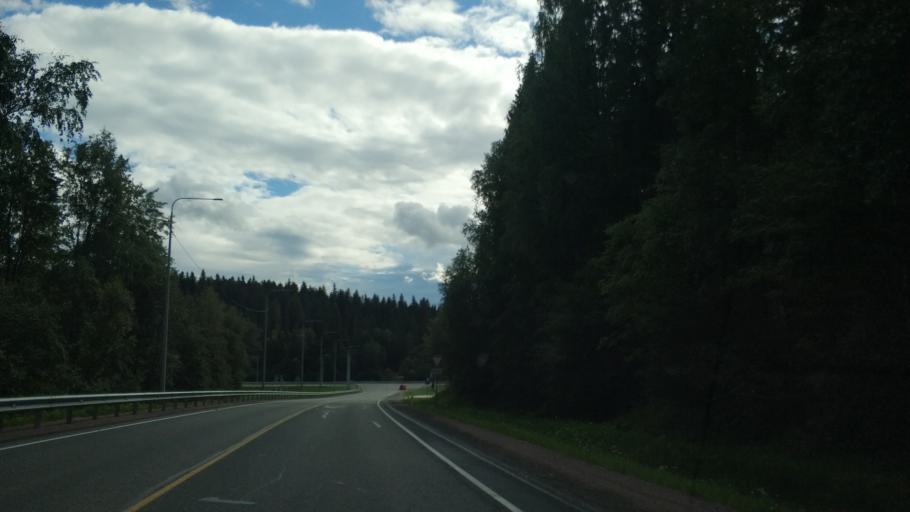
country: RU
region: Republic of Karelia
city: Khelyulya
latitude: 61.7780
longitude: 30.6605
